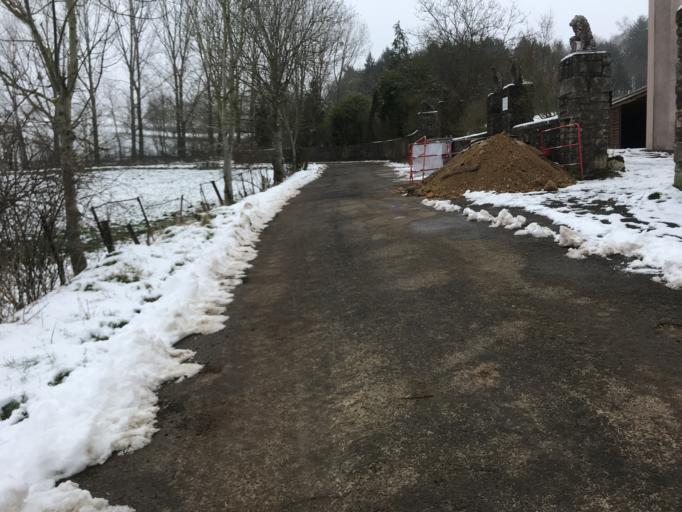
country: LU
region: Luxembourg
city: Belvaux
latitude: 49.4946
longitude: 5.9259
